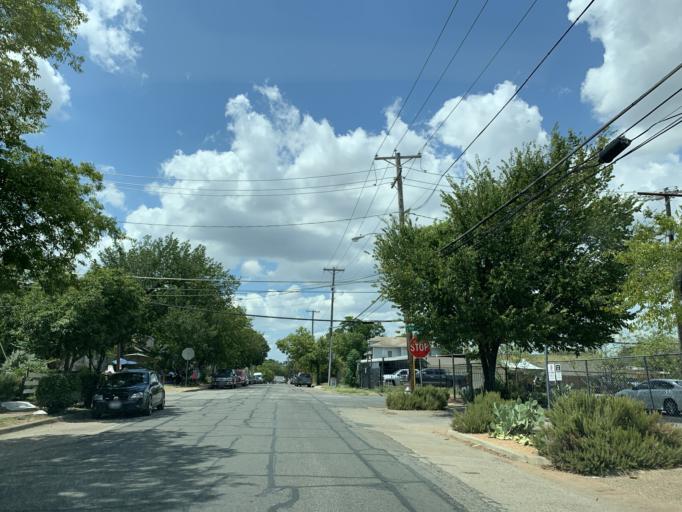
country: US
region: Texas
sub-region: Dallas County
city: Dallas
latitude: 32.7490
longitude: -96.8354
